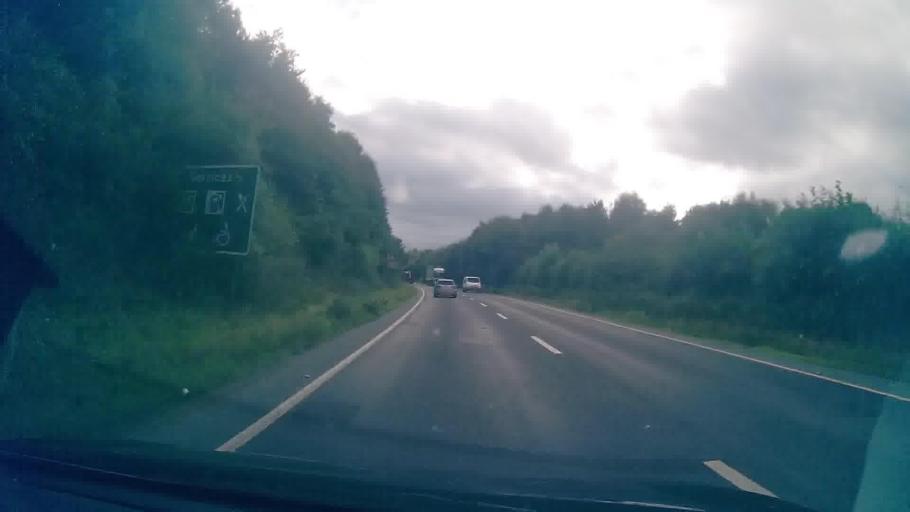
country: GB
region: England
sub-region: Shropshire
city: Whitchurch
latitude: 52.9749
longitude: -2.7076
